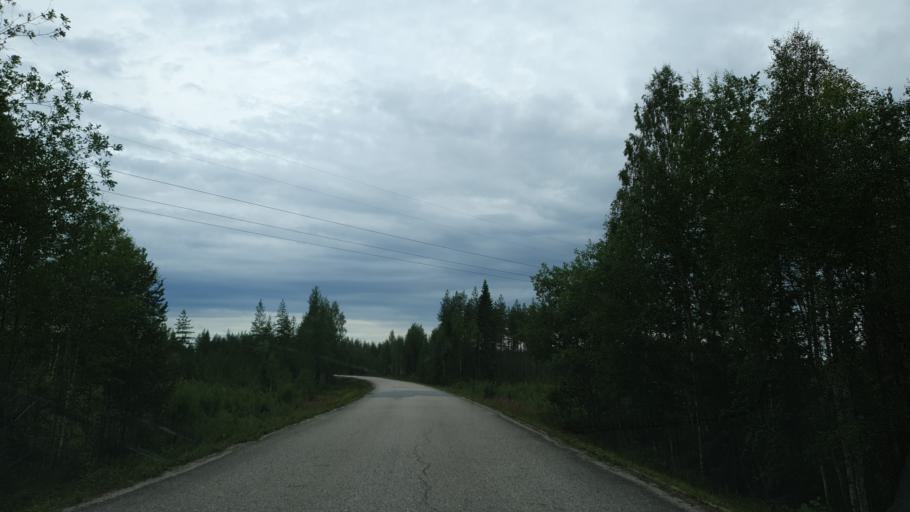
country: FI
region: Kainuu
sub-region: Kehys-Kainuu
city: Kuhmo
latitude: 64.3503
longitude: 29.1352
